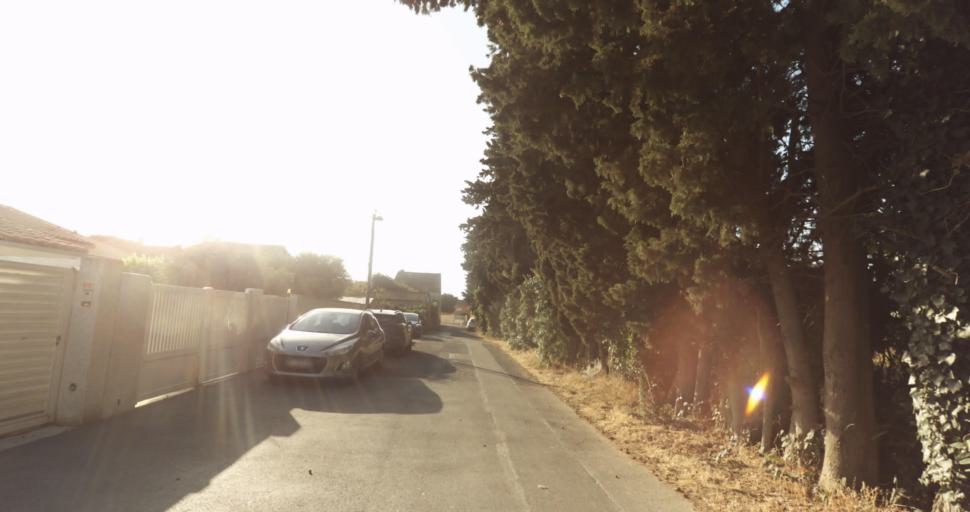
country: FR
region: Languedoc-Roussillon
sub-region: Departement des Pyrenees-Orientales
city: Latour-Bas-Elne
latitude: 42.6032
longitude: 3.0004
